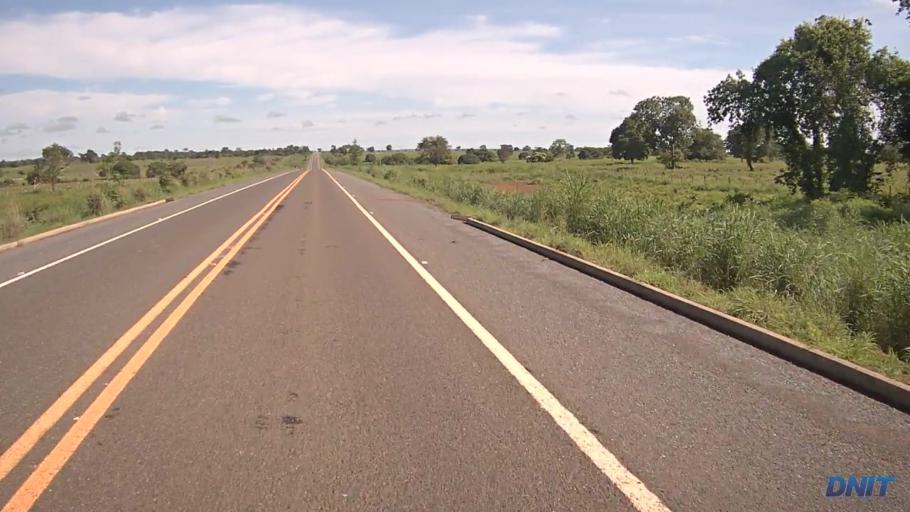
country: BR
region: Goias
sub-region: Sao Miguel Do Araguaia
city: Sao Miguel do Araguaia
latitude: -13.4586
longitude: -50.1183
